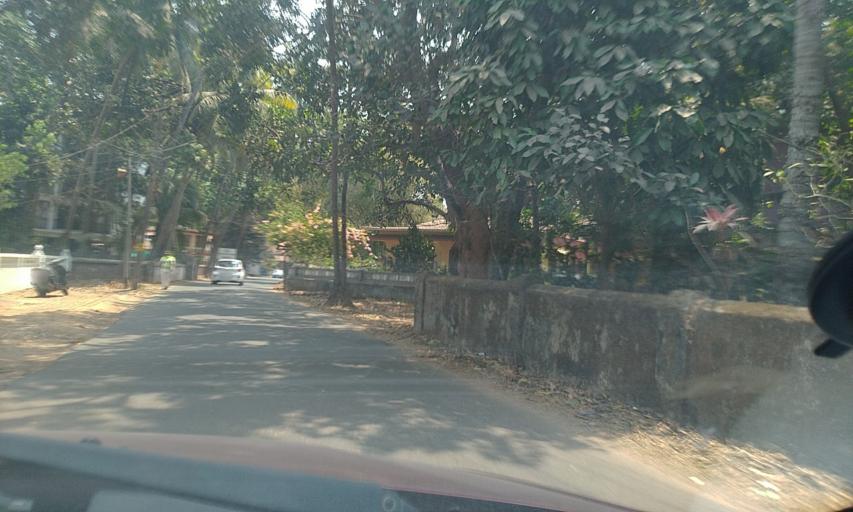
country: IN
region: Goa
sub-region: North Goa
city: Saligao
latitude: 15.5528
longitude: 73.7808
